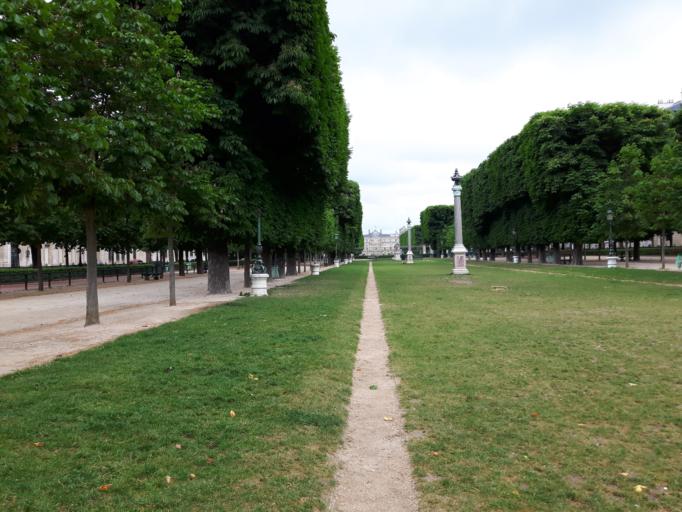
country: FR
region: Ile-de-France
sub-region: Paris
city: Paris
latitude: 48.8429
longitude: 2.3368
